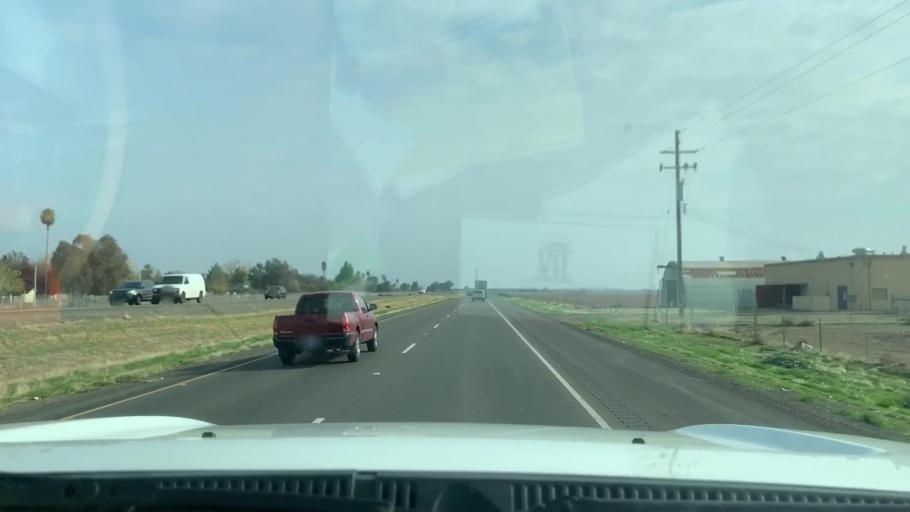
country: US
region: California
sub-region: Kings County
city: Lemoore Station
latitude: 36.2554
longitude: -119.8854
